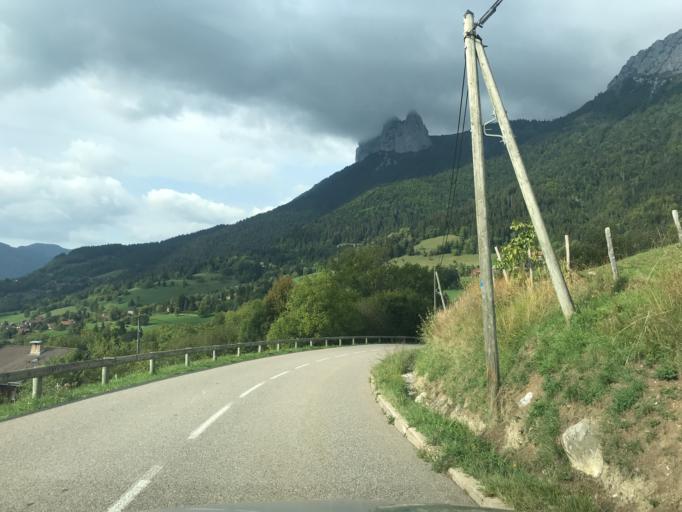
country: FR
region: Rhone-Alpes
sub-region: Departement de la Haute-Savoie
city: Talloires
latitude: 45.8289
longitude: 6.2379
